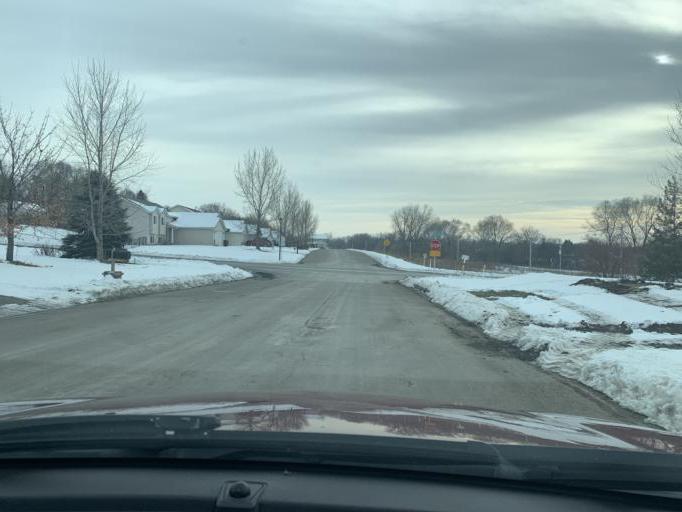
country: US
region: Minnesota
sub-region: Washington County
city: Saint Paul Park
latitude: 44.8427
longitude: -92.9929
